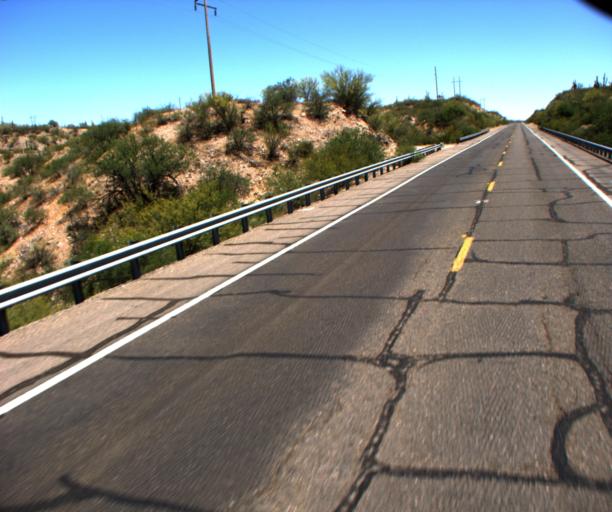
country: US
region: Arizona
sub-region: Pinal County
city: Mammoth
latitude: 32.7656
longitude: -110.6556
